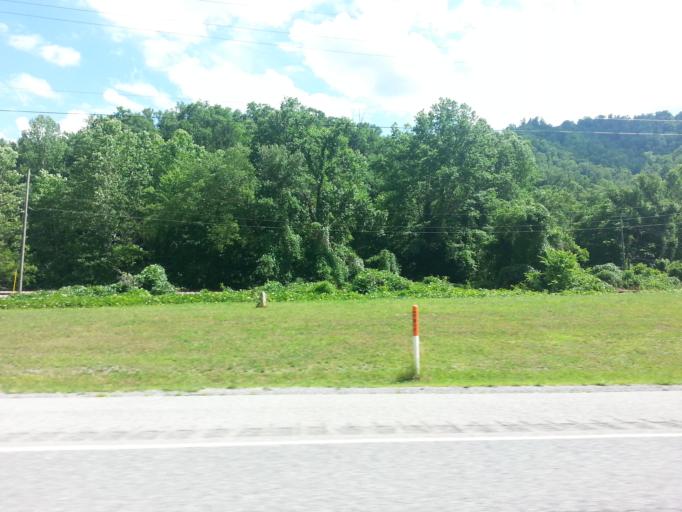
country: US
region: Kentucky
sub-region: Harlan County
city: Harlan
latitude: 36.8006
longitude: -83.2698
